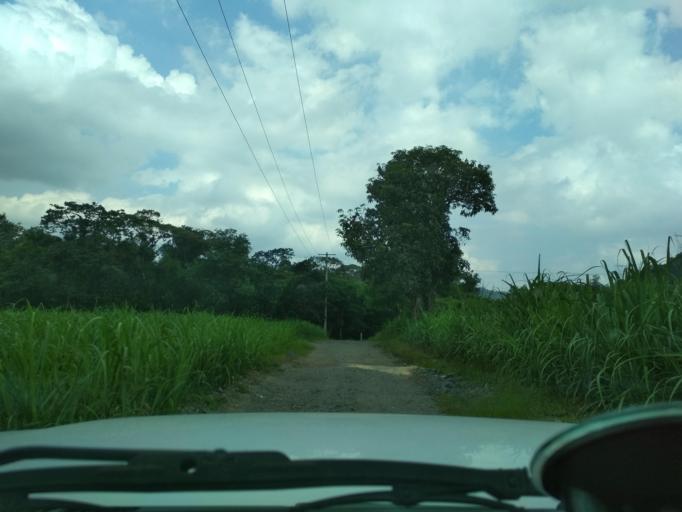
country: MX
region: Veracruz
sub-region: Ixtaczoquitlan
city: Buenavista
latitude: 18.9018
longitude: -97.0270
